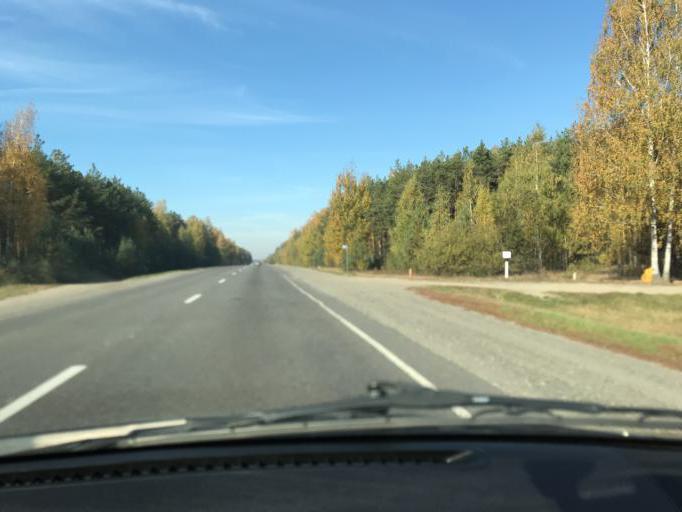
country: BY
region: Brest
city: Luninyets
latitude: 52.2693
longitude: 26.9999
